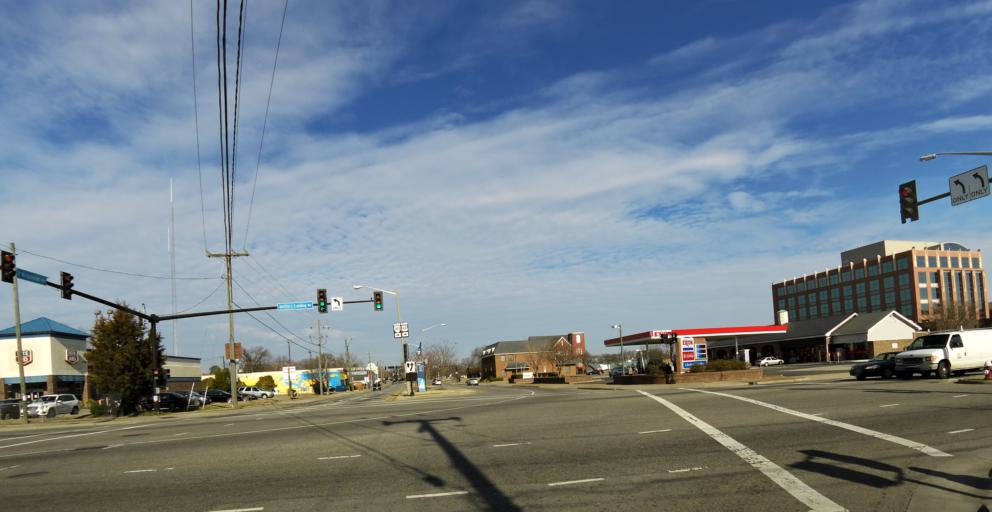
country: US
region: Virginia
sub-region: City of Hampton
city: Hampton
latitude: 37.0242
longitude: -76.3498
